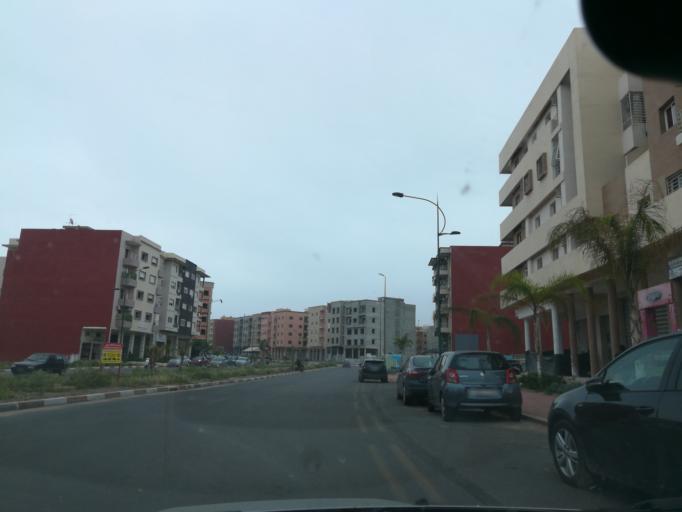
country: MA
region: Marrakech-Tensift-Al Haouz
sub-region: Marrakech
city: Marrakesh
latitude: 31.6747
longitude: -8.0233
